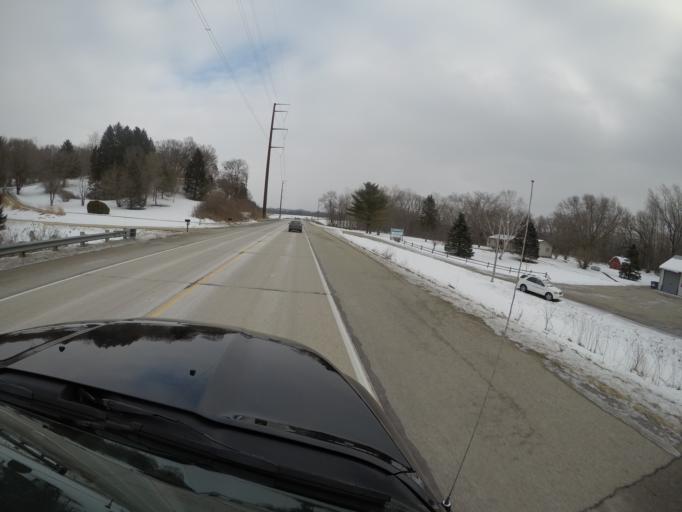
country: US
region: Wisconsin
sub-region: Trempealeau County
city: Galesville
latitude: 44.0716
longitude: -91.3094
